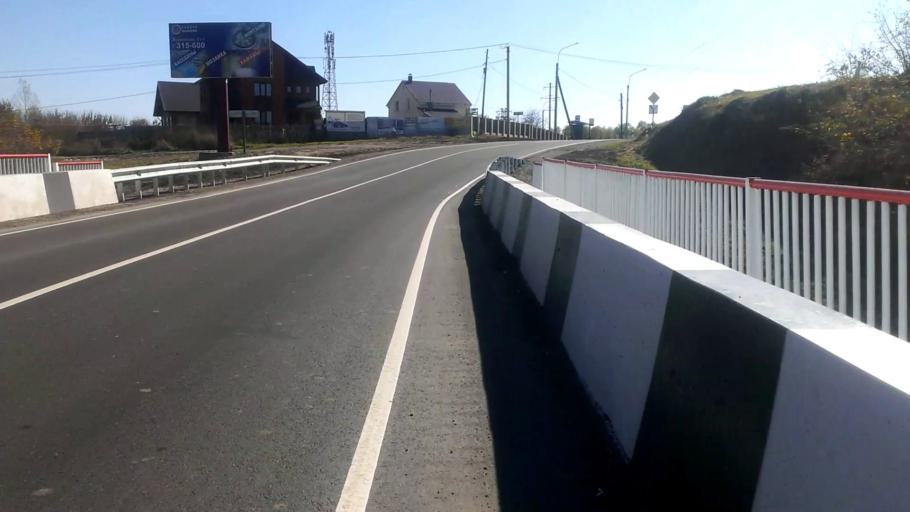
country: RU
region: Altai Krai
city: Sannikovo
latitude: 53.3196
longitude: 83.9442
